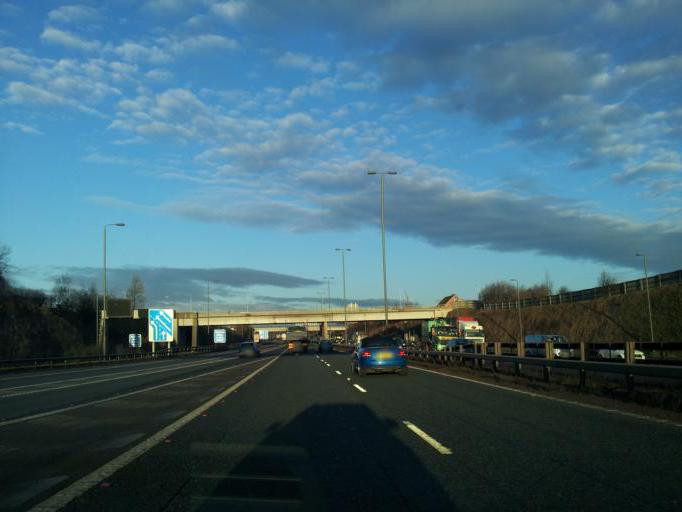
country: GB
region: England
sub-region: City and Borough of Leeds
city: Lofthouse
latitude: 53.7324
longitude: -1.5194
